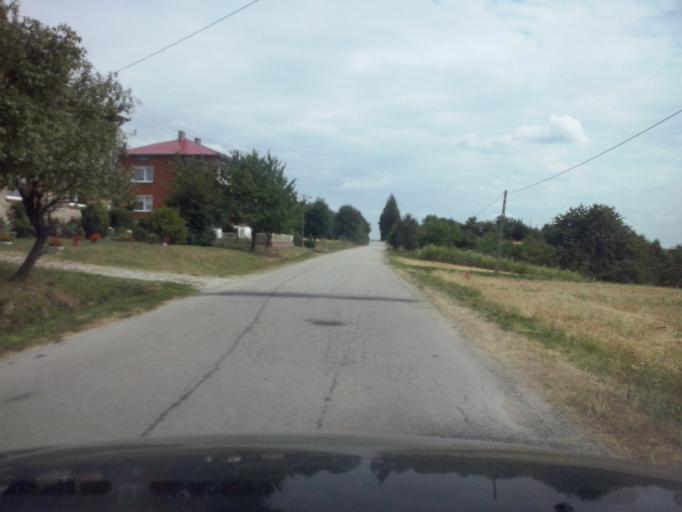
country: PL
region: Swietokrzyskie
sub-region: Powiat kielecki
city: Lagow
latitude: 50.7176
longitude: 21.1235
